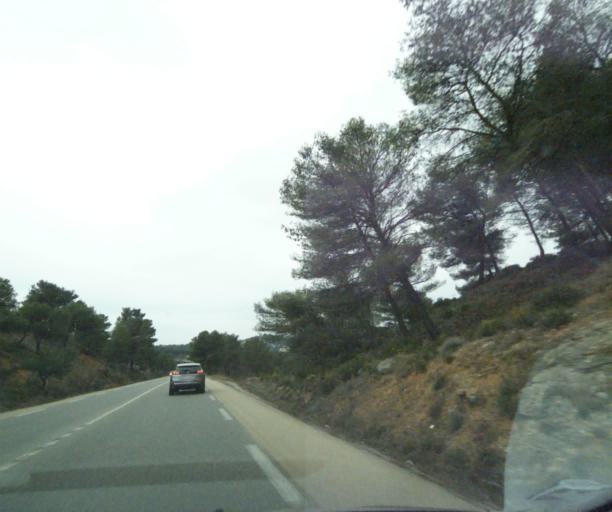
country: FR
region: Provence-Alpes-Cote d'Azur
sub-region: Departement des Bouches-du-Rhone
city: Venelles
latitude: 43.6144
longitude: 5.5025
